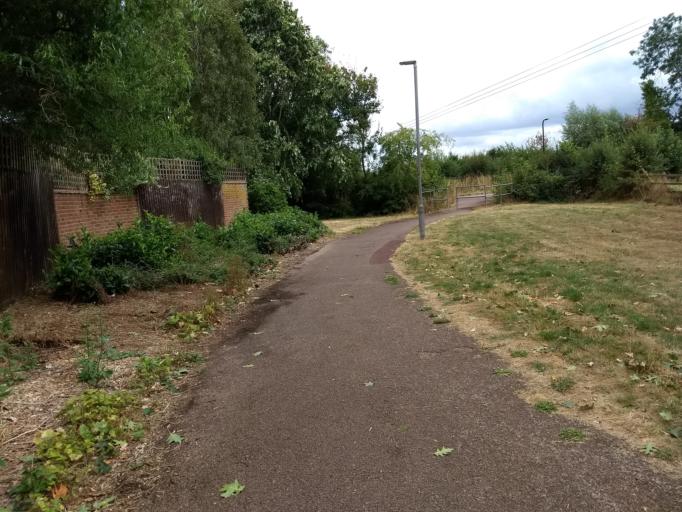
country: GB
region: England
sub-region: Milton Keynes
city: Newport Pagnell
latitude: 52.0760
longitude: -0.7253
